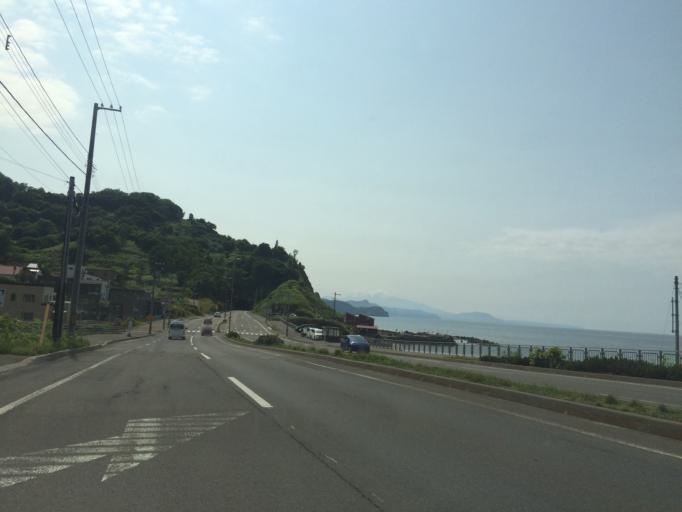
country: JP
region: Hokkaido
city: Otaru
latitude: 43.2106
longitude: 140.9155
